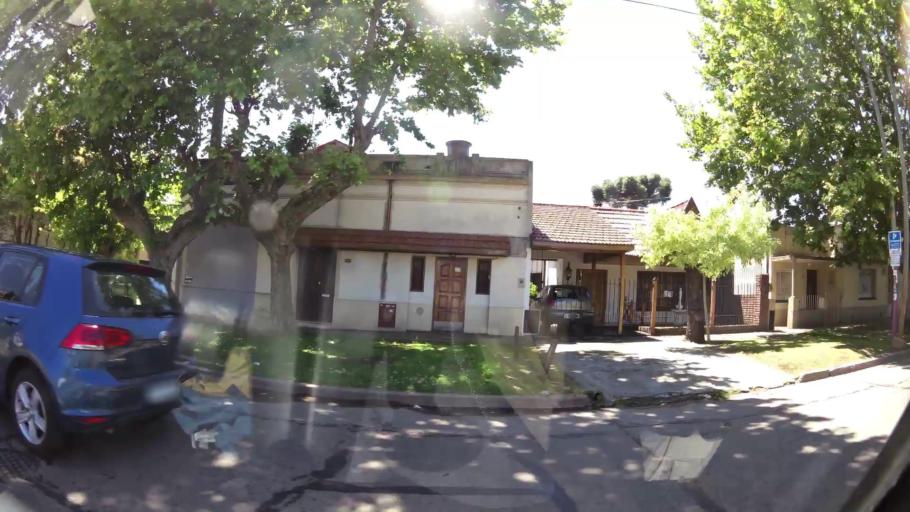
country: AR
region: Buenos Aires
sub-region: Partido de Quilmes
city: Quilmes
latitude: -34.7266
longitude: -58.2738
